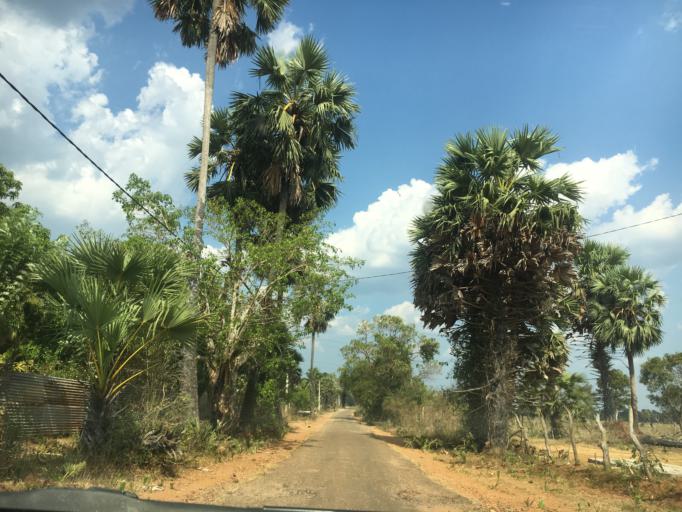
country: LK
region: Northern Province
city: Kilinochchi
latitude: 9.1390
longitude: 80.4500
